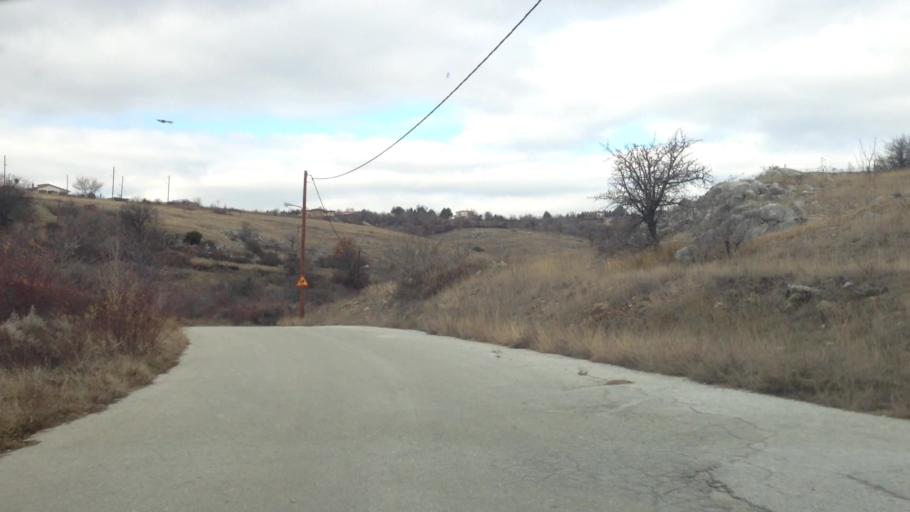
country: GR
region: West Macedonia
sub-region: Nomos Kozanis
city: Kozani
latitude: 40.2950
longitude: 21.7718
